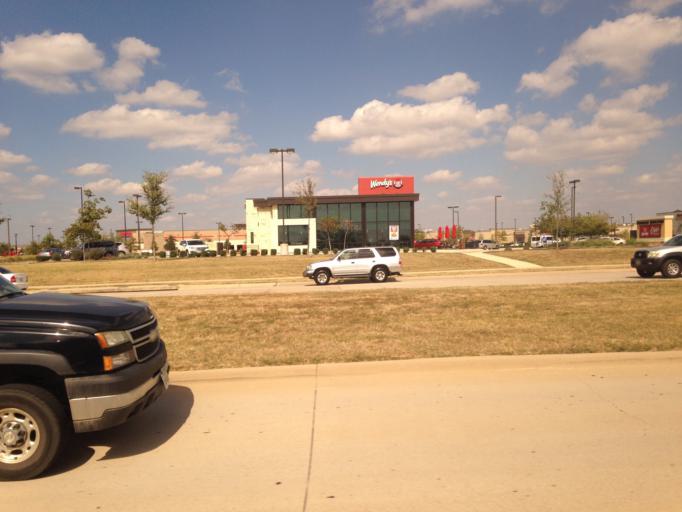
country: US
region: Texas
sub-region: Tarrant County
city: Blue Mound
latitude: 32.8984
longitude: -97.3200
